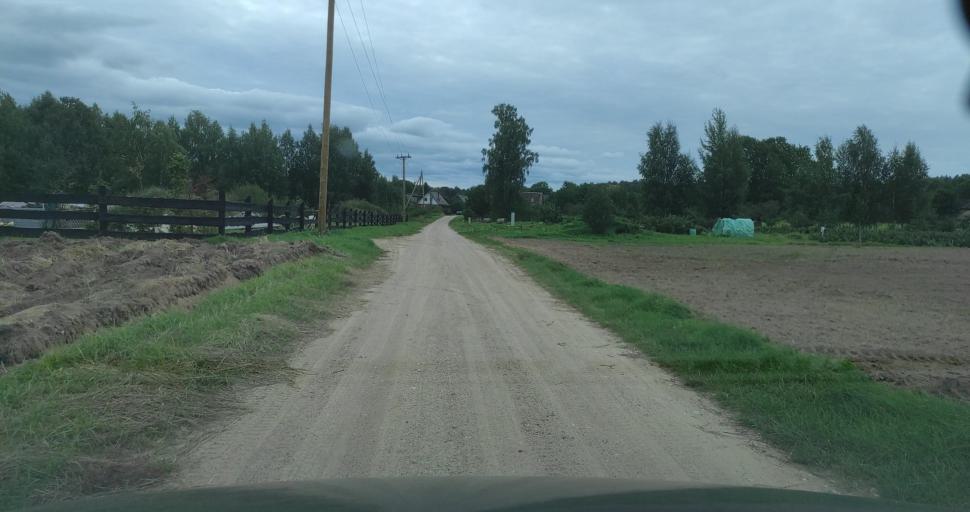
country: LV
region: Kuldigas Rajons
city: Kuldiga
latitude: 56.9261
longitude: 21.9666
